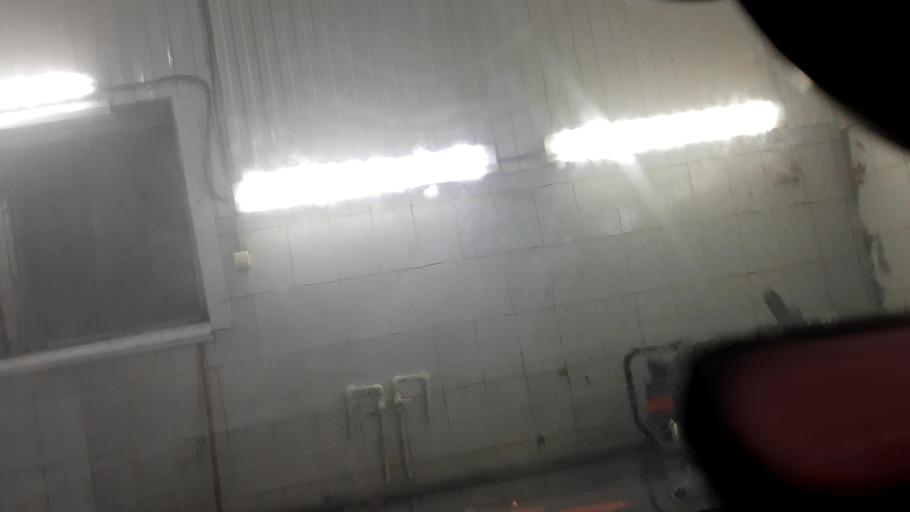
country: RU
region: Bashkortostan
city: Mikhaylovka
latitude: 54.7964
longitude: 55.8798
